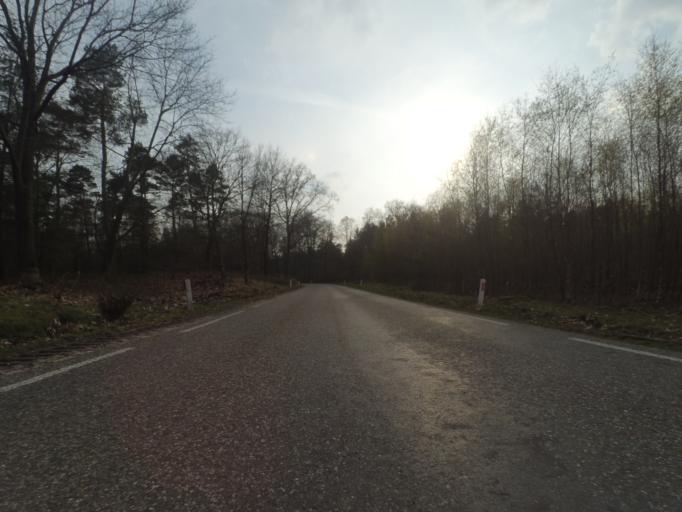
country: NL
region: Gelderland
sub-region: Gemeente Apeldoorn
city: Beekbergen
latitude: 52.1416
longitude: 5.9318
